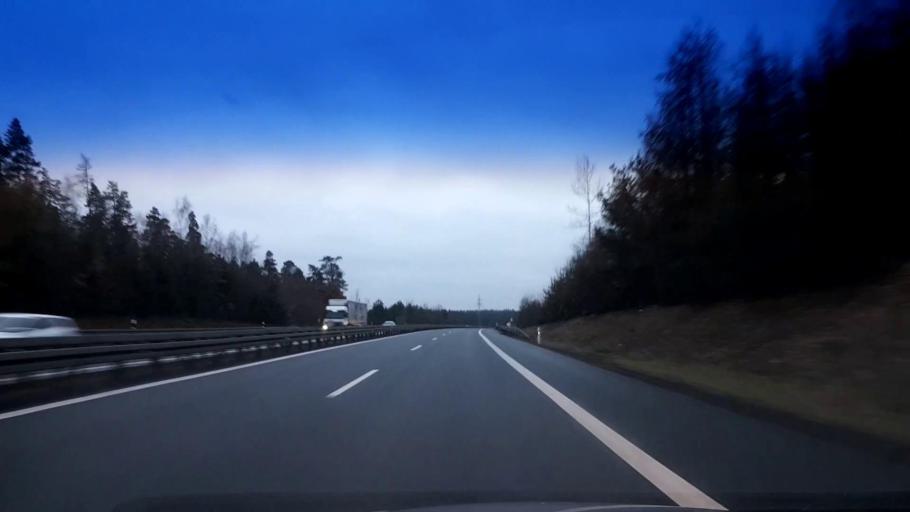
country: DE
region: Bavaria
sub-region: Upper Palatinate
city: Wiesau
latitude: 49.8943
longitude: 12.2190
